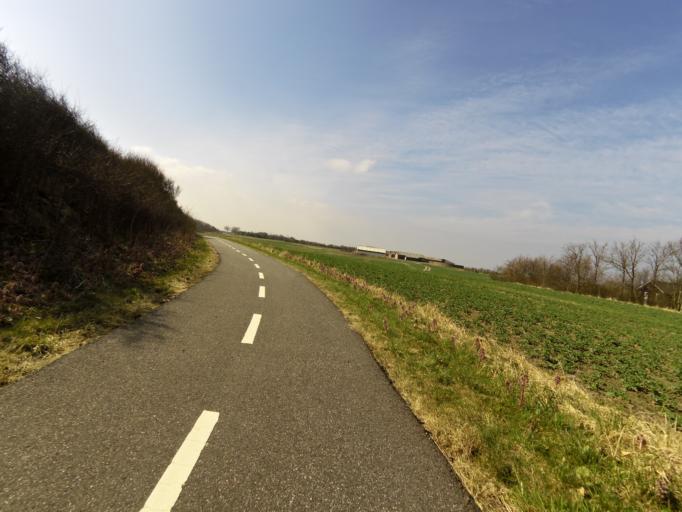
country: DK
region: Central Jutland
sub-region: Holstebro Kommune
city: Vinderup
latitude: 56.4698
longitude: 8.7064
